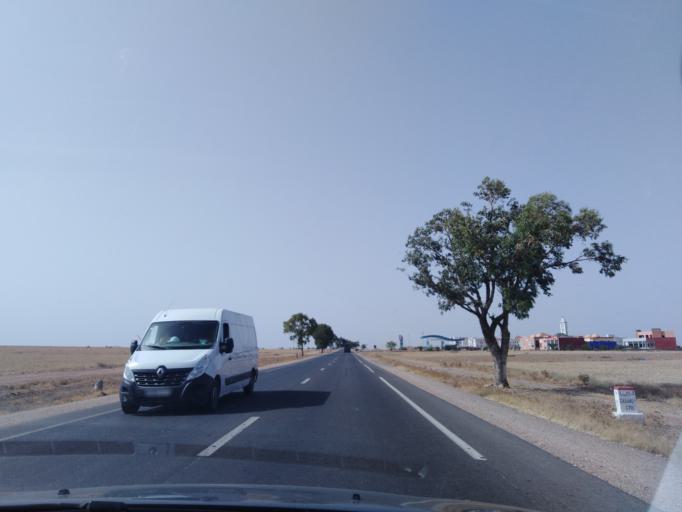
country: MA
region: Marrakech-Tensift-Al Haouz
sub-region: Kelaa-Des-Sraghna
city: Sidi Bou Othmane
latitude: 32.2153
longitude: -7.9568
